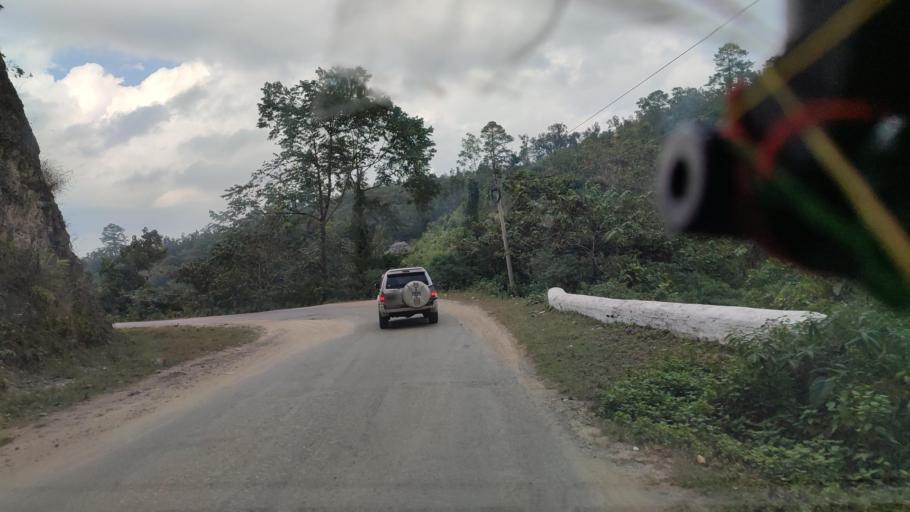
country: MM
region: Shan
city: Taunggyi
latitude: 21.1904
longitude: 97.6089
